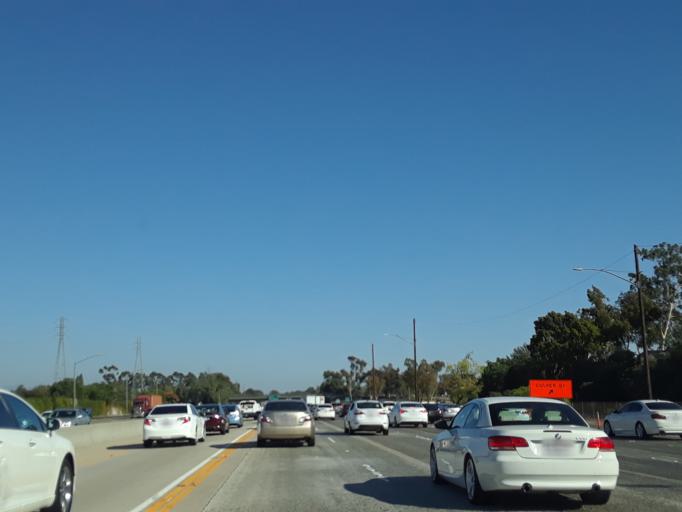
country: US
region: California
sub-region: Orange County
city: Irvine
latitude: 33.6713
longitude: -117.8285
